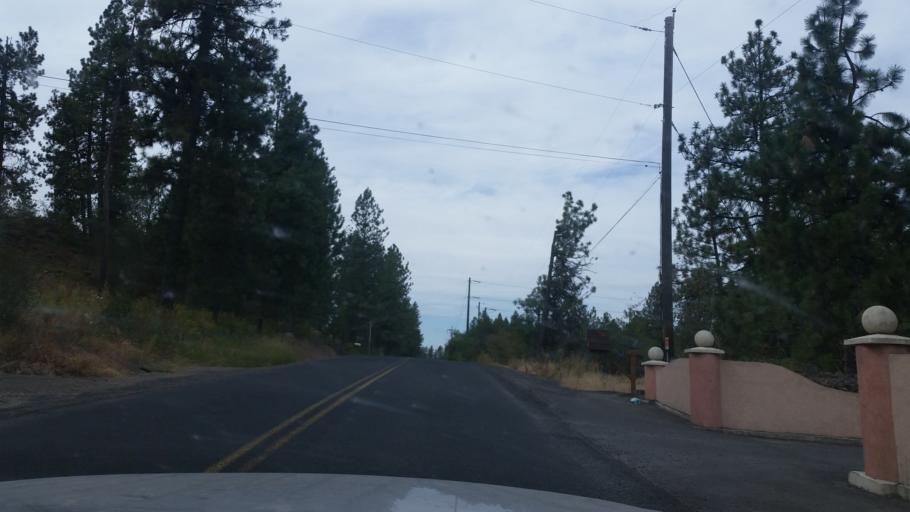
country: US
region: Washington
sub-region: Spokane County
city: Spokane
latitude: 47.6555
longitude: -117.4895
